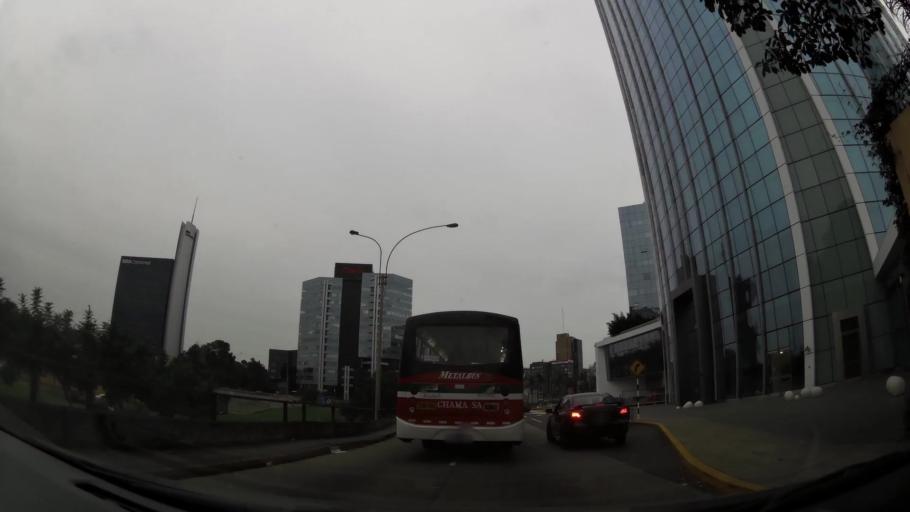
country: PE
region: Lima
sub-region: Lima
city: San Luis
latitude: -12.0917
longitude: -77.0237
